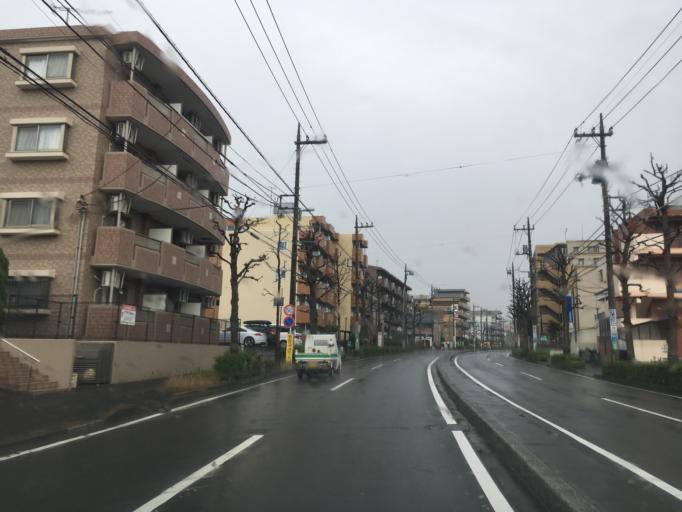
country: JP
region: Tokyo
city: Hino
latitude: 35.6321
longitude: 139.4536
